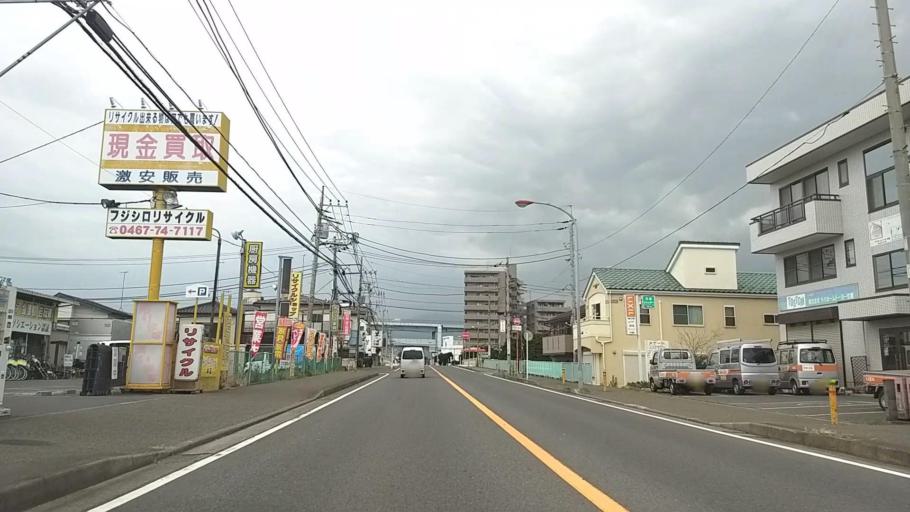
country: JP
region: Kanagawa
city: Chigasaki
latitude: 35.3714
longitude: 139.3781
